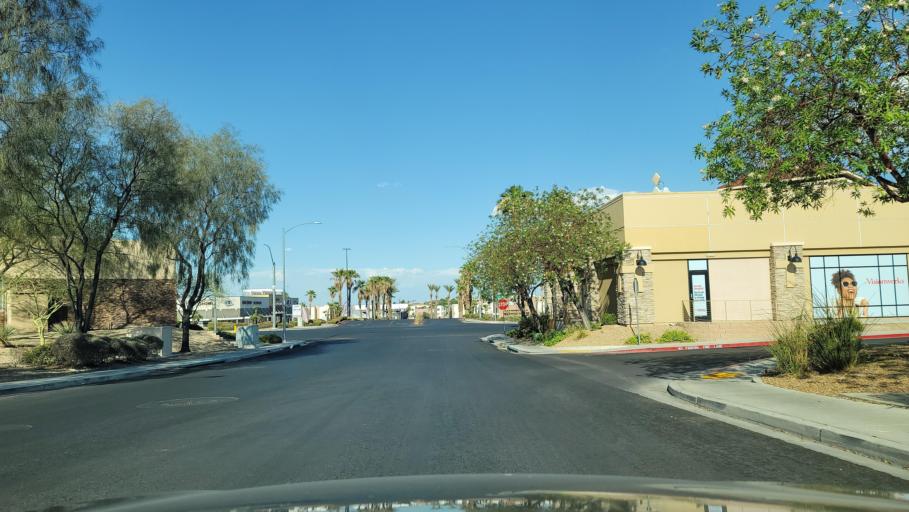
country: US
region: Nevada
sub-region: Clark County
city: Summerlin South
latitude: 36.0963
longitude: -115.2983
